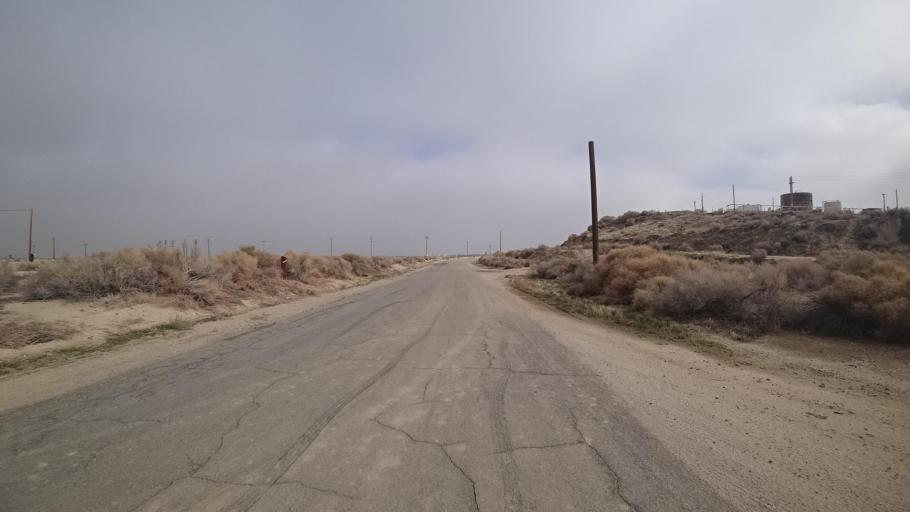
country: US
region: California
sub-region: Kern County
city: Maricopa
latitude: 35.0385
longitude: -119.3778
